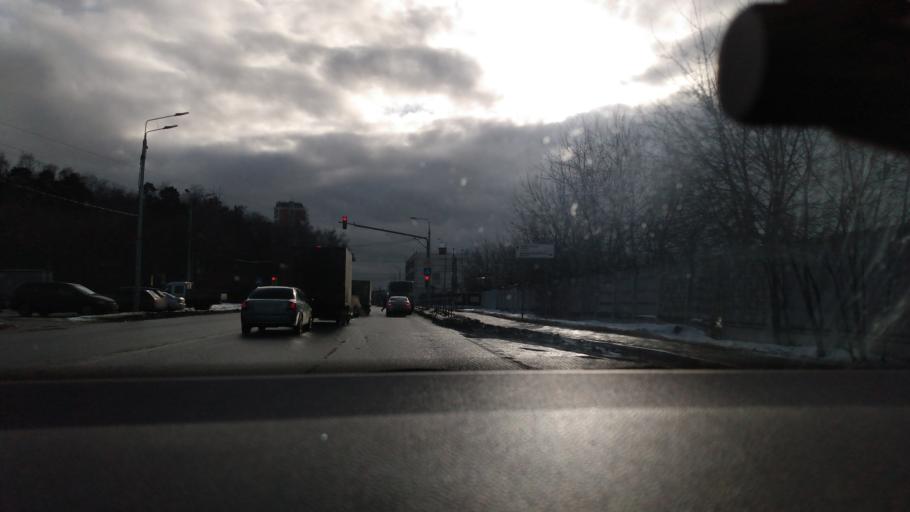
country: RU
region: Moskovskaya
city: Balashikha
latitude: 55.8209
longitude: 37.9533
